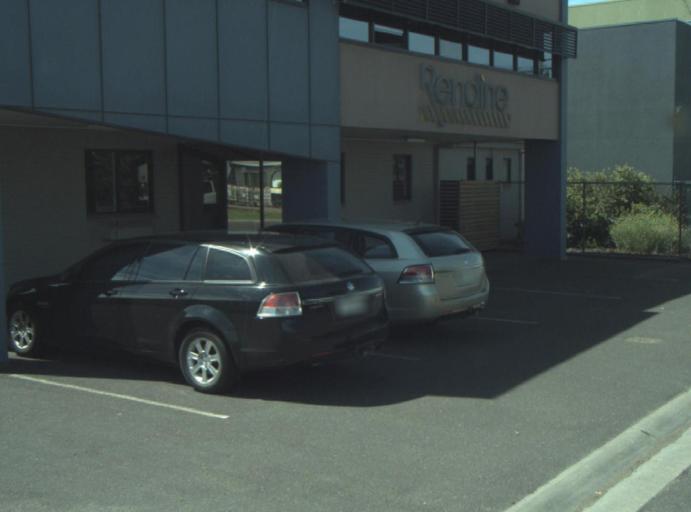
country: AU
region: Victoria
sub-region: Greater Geelong
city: East Geelong
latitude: -38.1656
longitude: 144.4091
